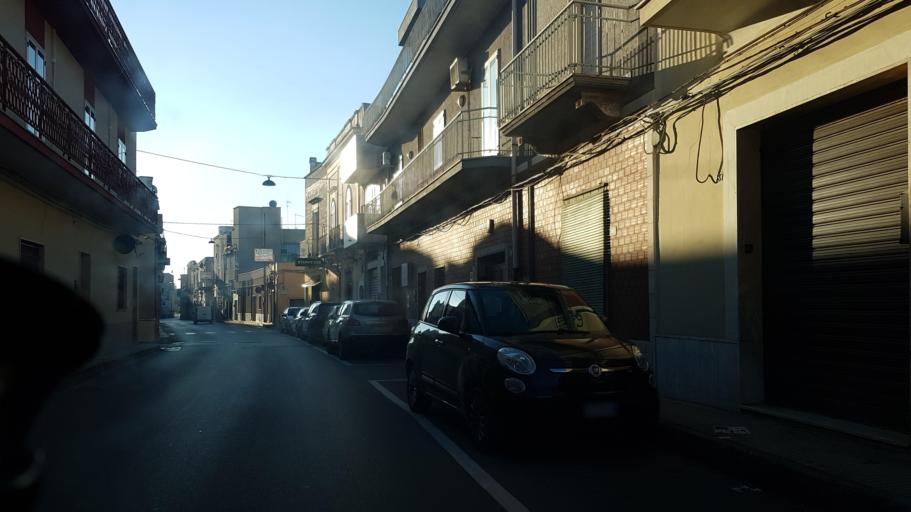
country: IT
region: Apulia
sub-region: Provincia di Brindisi
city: Latiano
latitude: 40.5528
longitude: 17.7208
